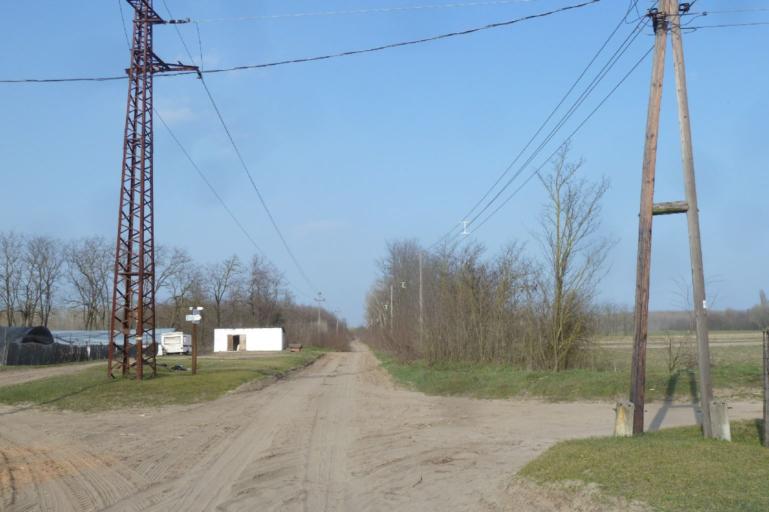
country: HU
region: Bacs-Kiskun
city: Lajosmizse
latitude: 46.9947
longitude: 19.5651
